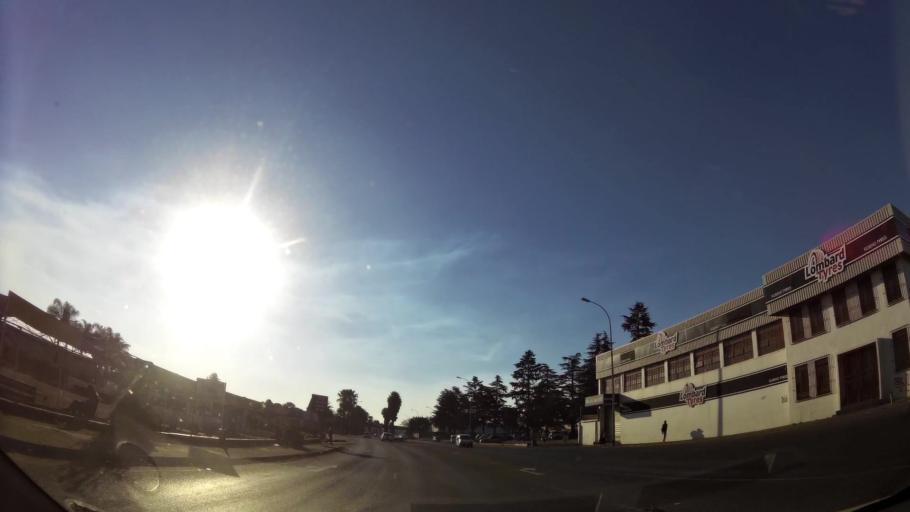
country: ZA
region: Gauteng
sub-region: City of Johannesburg Metropolitan Municipality
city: Roodepoort
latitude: -26.1576
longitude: 27.8682
